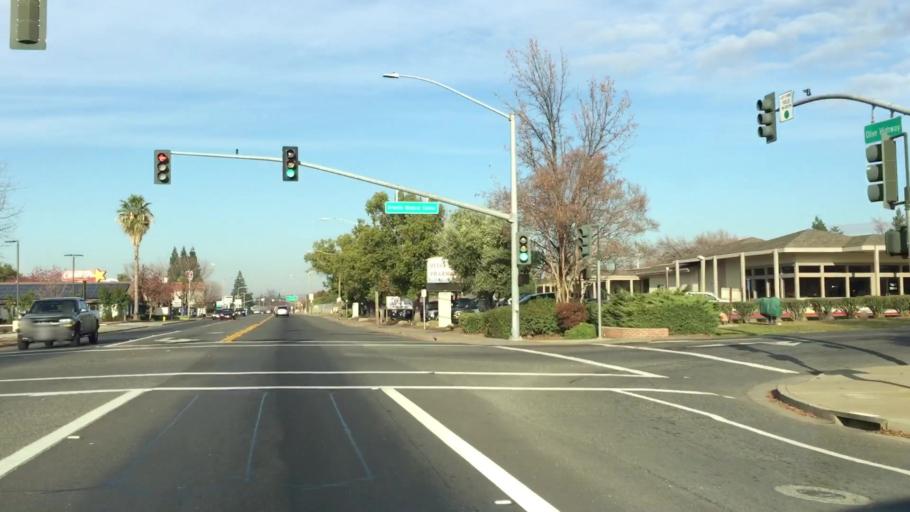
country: US
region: California
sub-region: Butte County
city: South Oroville
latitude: 39.5041
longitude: -121.5414
